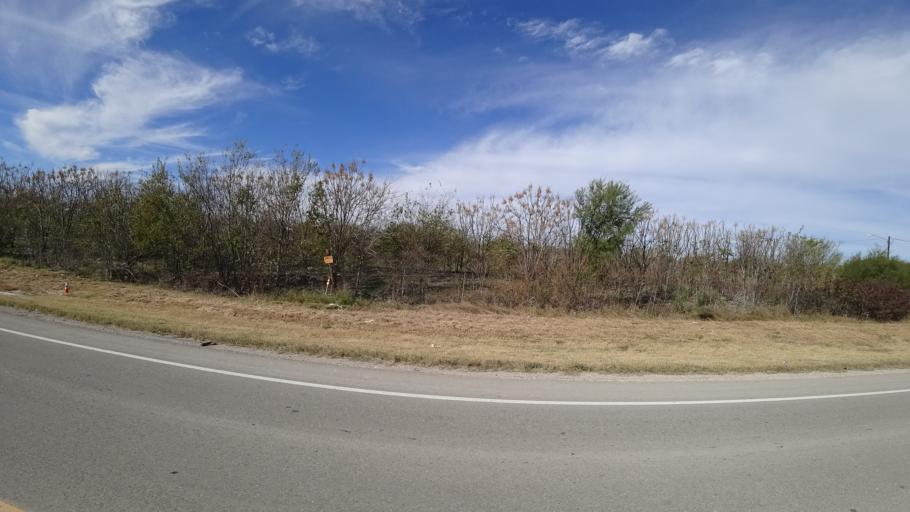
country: US
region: Texas
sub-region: Travis County
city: Onion Creek
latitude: 30.1172
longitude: -97.6921
